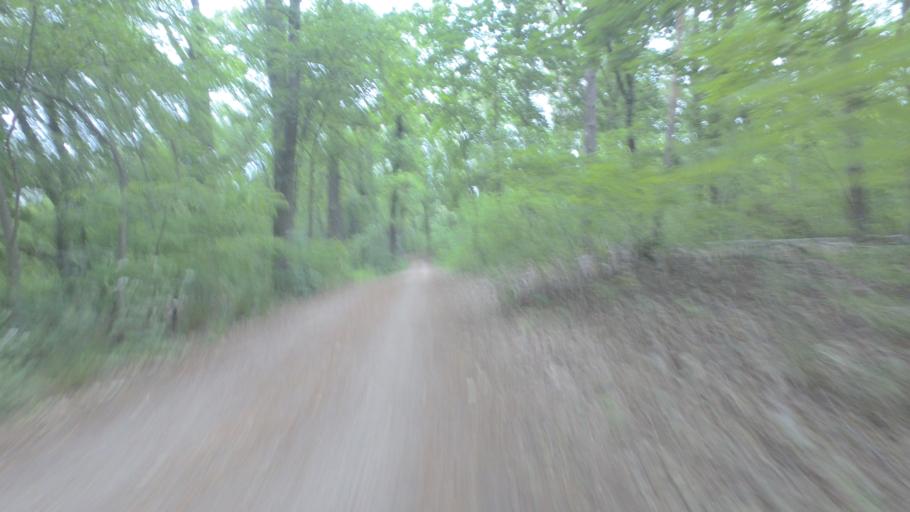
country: DE
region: Brandenburg
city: Rangsdorf
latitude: 52.3036
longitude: 13.4176
